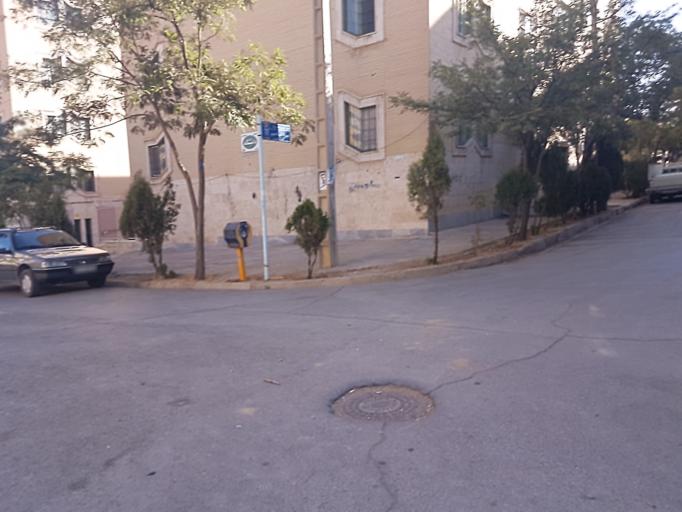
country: IR
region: Markazi
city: Arak
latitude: 34.0696
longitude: 49.6765
